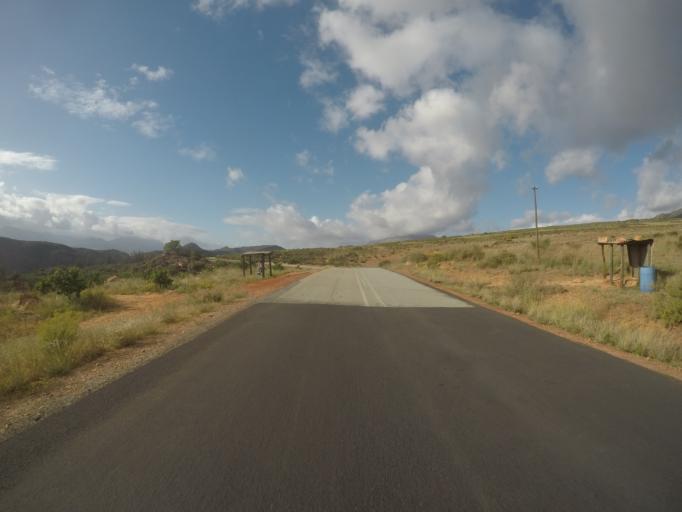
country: ZA
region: Western Cape
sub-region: West Coast District Municipality
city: Clanwilliam
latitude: -32.4240
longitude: 18.9346
